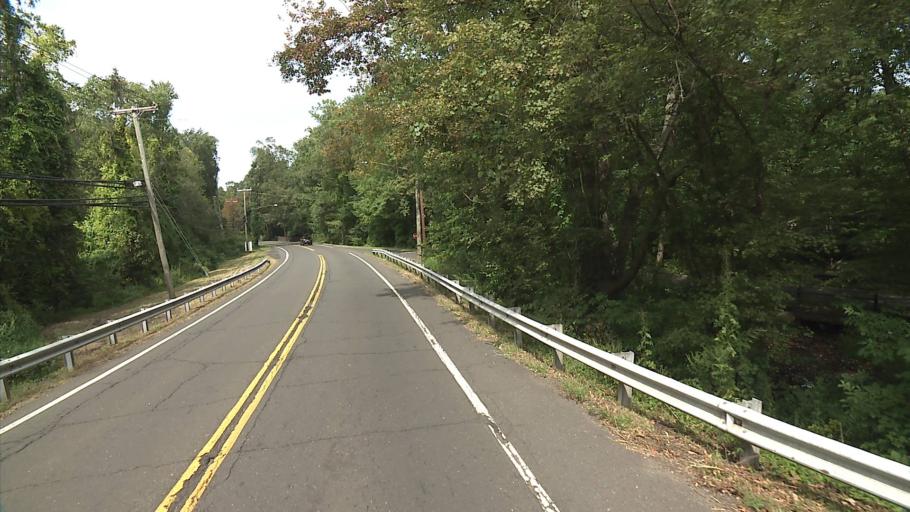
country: US
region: Connecticut
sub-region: Fairfield County
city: North Stamford
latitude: 41.1247
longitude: -73.5735
